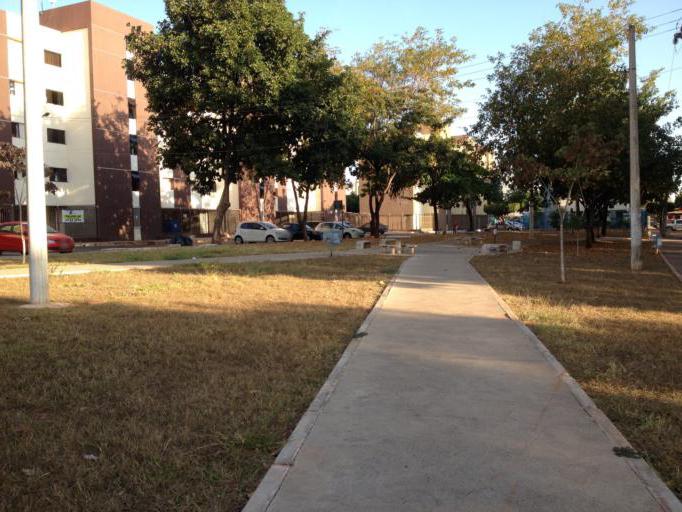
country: BR
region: Federal District
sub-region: Brasilia
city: Brasilia
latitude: -15.7955
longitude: -47.9377
